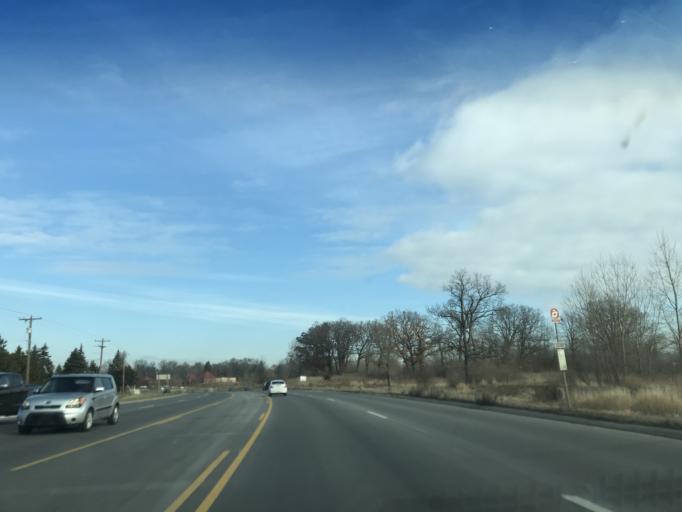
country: US
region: Michigan
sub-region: Oakland County
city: Auburn Hills
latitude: 42.6716
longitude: -83.2543
